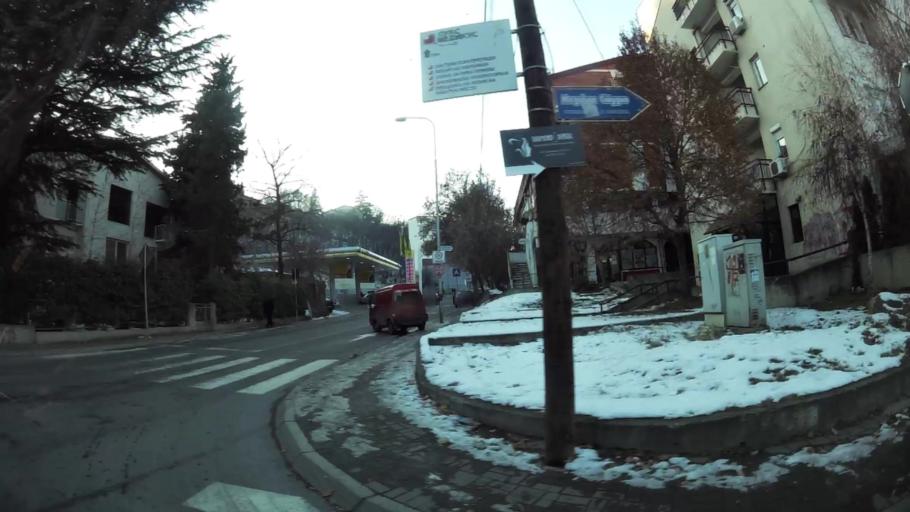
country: MK
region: Karpos
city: Skopje
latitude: 41.9946
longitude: 21.3967
